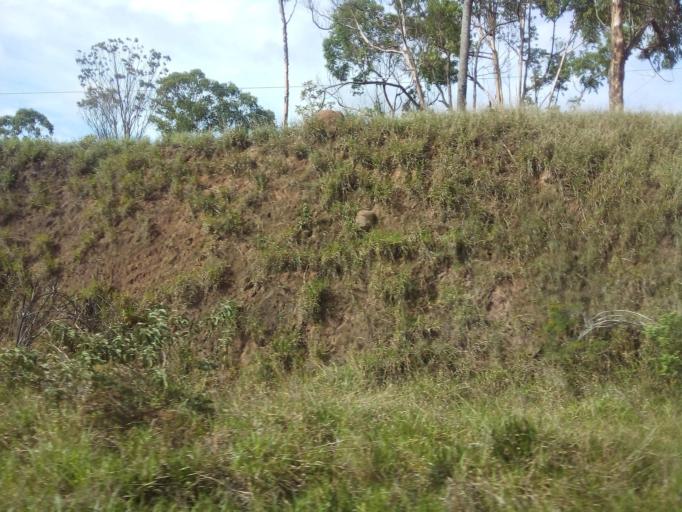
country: BR
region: Minas Gerais
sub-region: Raposos
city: Raposos
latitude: -19.8734
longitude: -43.7836
